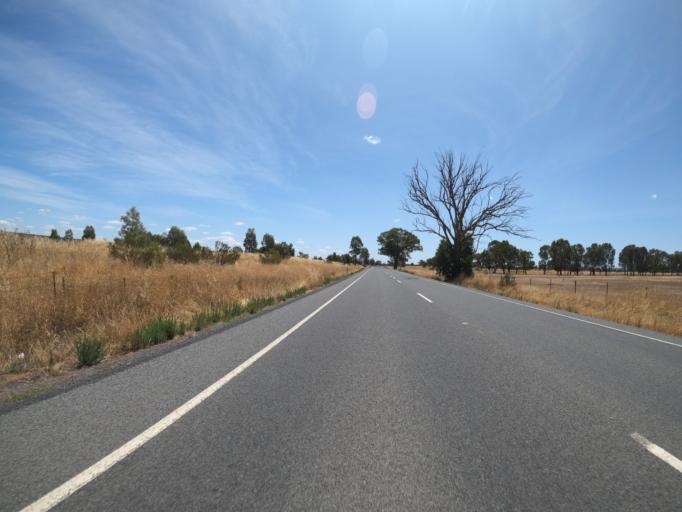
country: AU
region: Victoria
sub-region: Benalla
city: Benalla
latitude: -36.5209
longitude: 146.0351
